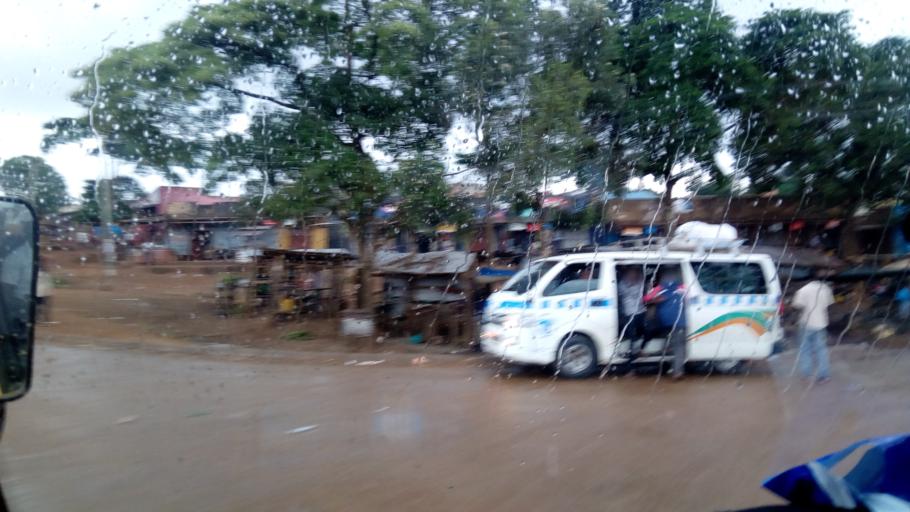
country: UG
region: Central Region
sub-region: Mityana District
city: Mityana
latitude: 0.4370
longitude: 31.9109
